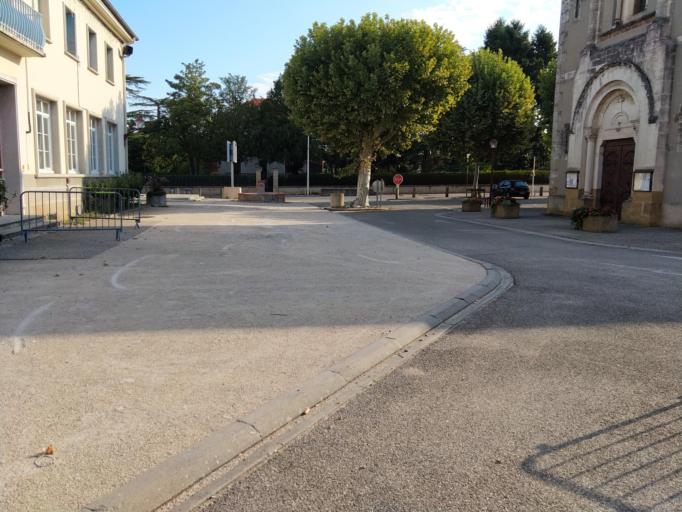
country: FR
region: Rhone-Alpes
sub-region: Departement de la Drome
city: Saint-Sorlin-en-Valloire
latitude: 45.3227
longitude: 4.9945
